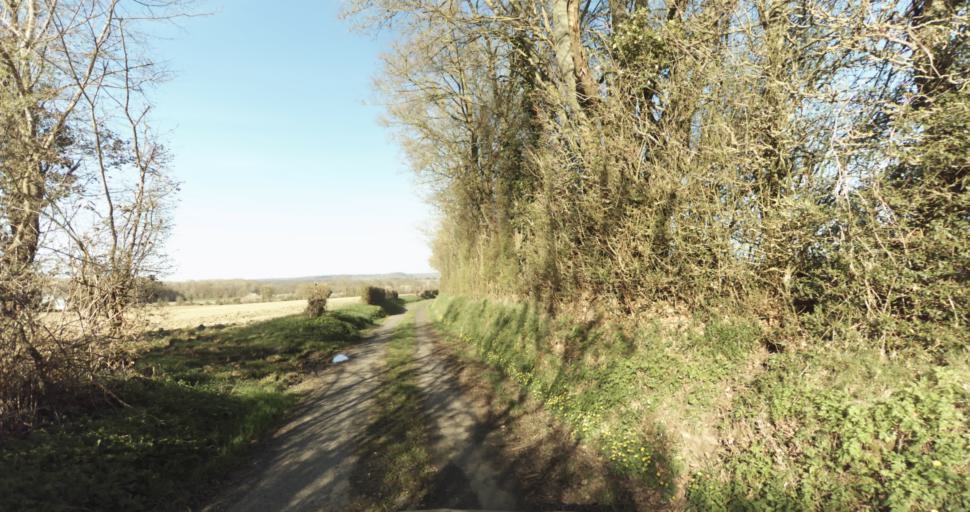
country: FR
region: Lower Normandy
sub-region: Departement du Calvados
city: Saint-Pierre-sur-Dives
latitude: 49.0446
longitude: 0.0423
